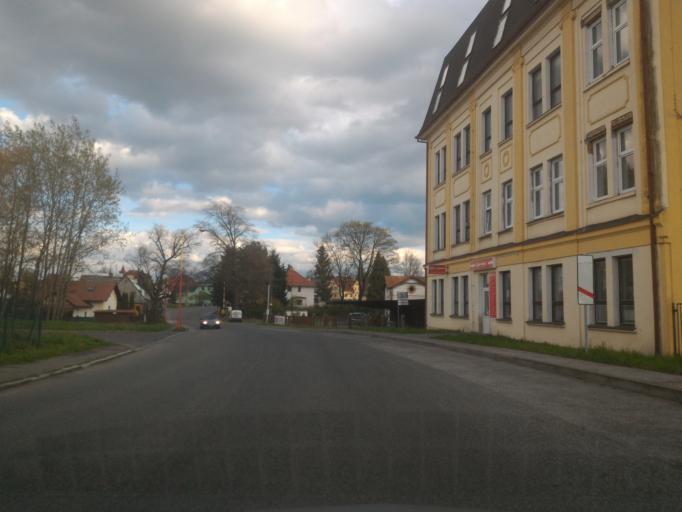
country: CZ
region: Ustecky
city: Varnsdorf
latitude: 50.8962
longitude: 14.6198
